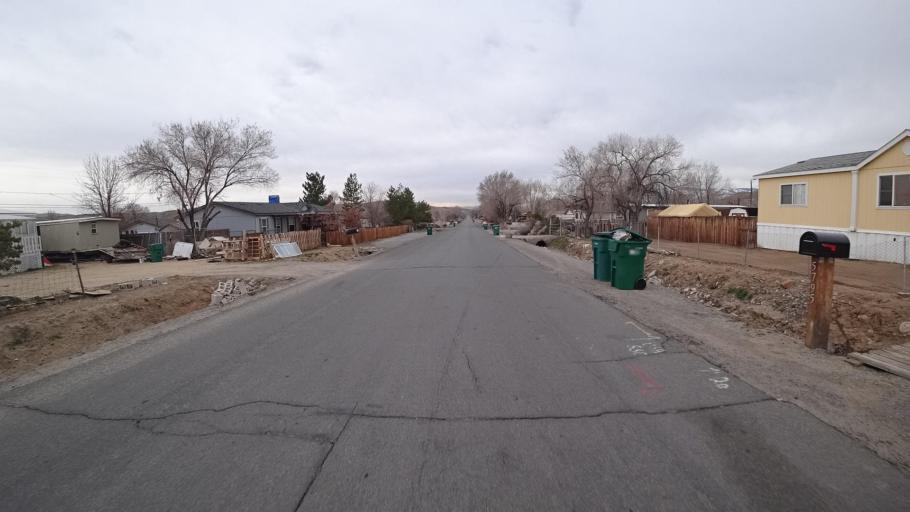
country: US
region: Nevada
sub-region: Washoe County
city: Sun Valley
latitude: 39.6036
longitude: -119.7711
